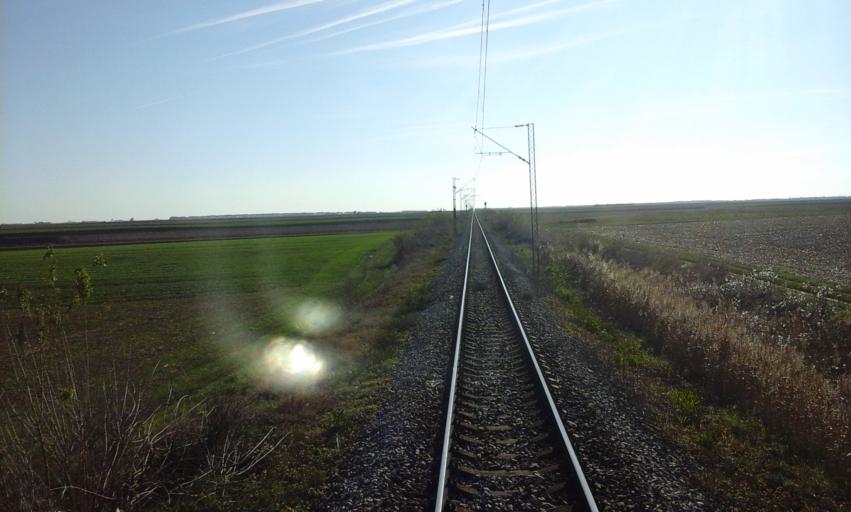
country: RS
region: Autonomna Pokrajina Vojvodina
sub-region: Severnobacki Okrug
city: Backa Topola
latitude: 45.9196
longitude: 19.6652
